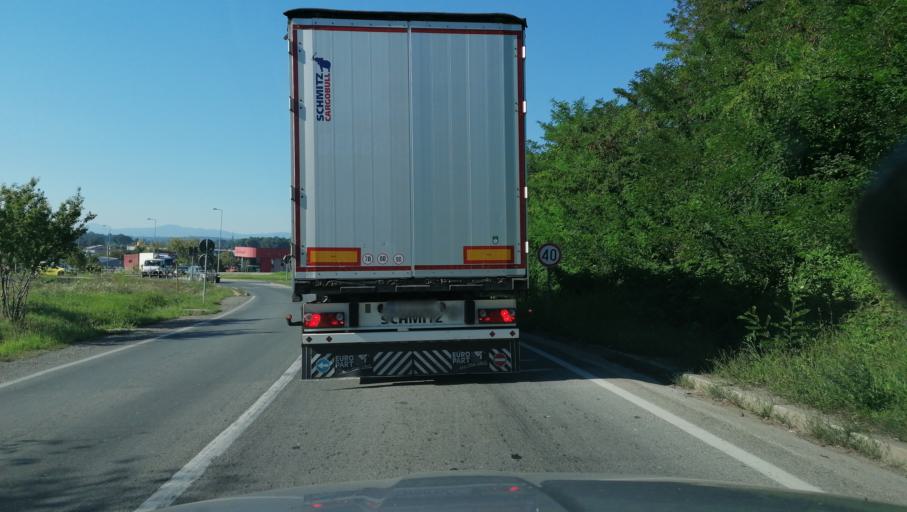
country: RS
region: Central Serbia
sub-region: Raski Okrug
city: Kraljevo
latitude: 43.7364
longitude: 20.6706
